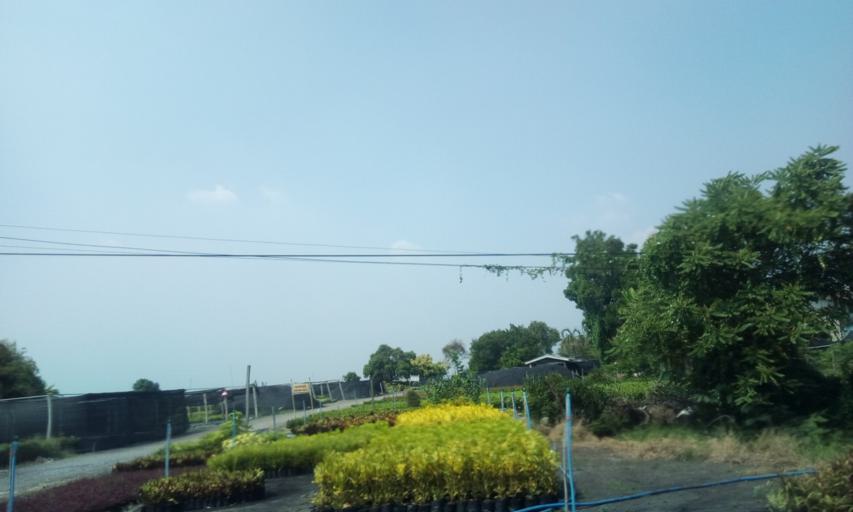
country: TH
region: Nakhon Nayok
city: Ongkharak
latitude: 14.1416
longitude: 100.9739
